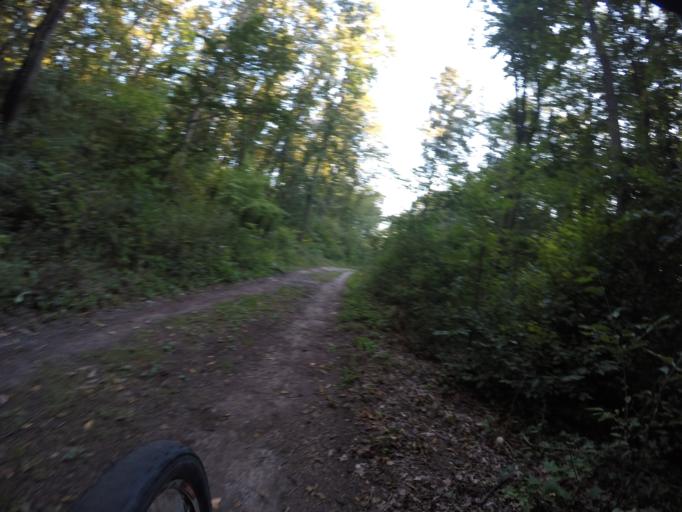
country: AT
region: Lower Austria
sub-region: Politischer Bezirk Bruck an der Leitha
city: Mannersdorf am Leithagebirge
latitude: 47.9587
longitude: 16.5934
